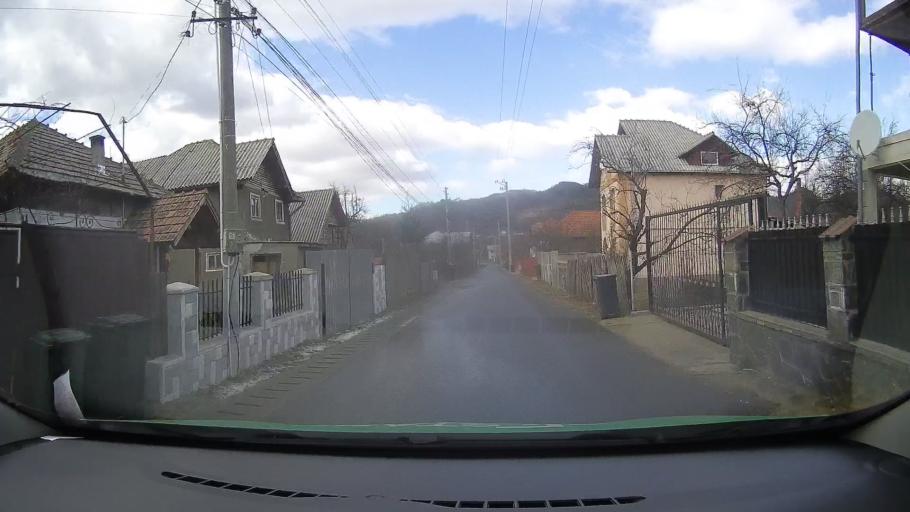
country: RO
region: Dambovita
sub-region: Comuna Buciumeni
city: Buciumeni
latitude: 45.1524
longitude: 25.4548
